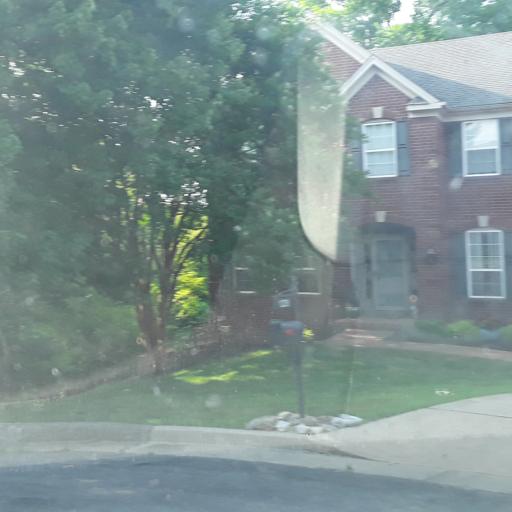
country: US
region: Tennessee
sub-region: Williamson County
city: Brentwood
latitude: 36.0549
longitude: -86.7505
